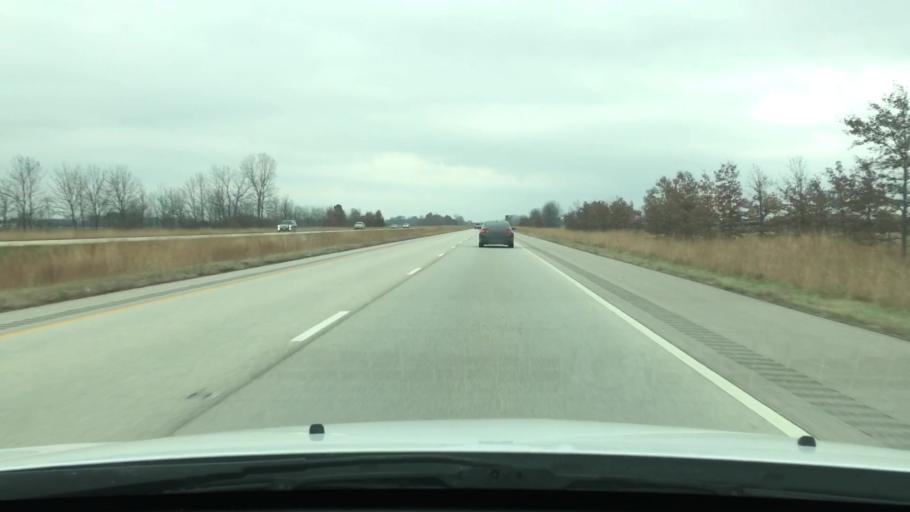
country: US
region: Illinois
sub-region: Sangamon County
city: Jerome
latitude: 39.7516
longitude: -89.7897
